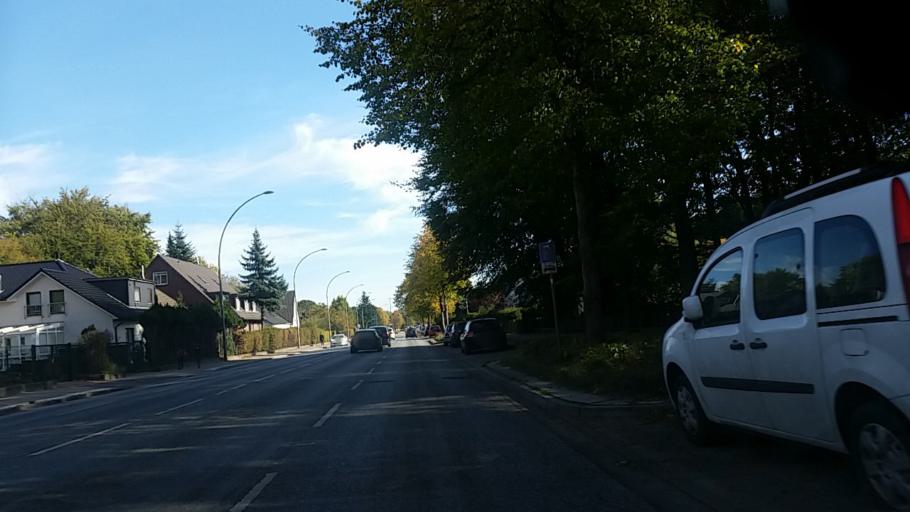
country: DE
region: Hamburg
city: Eidelstedt
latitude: 53.5931
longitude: 9.8875
